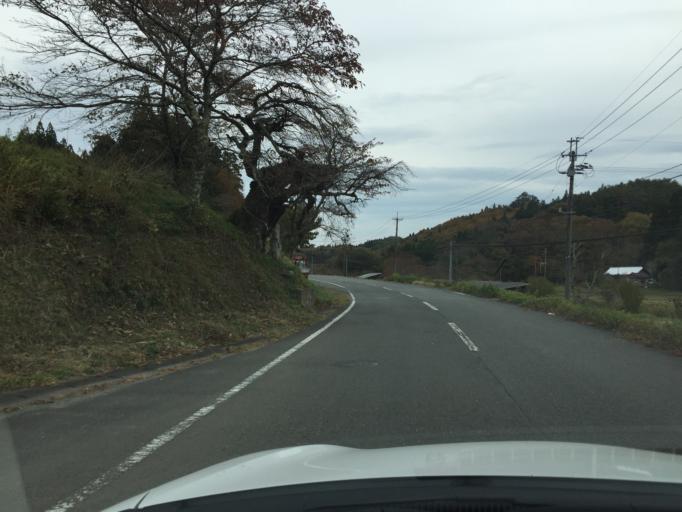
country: JP
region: Fukushima
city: Ishikawa
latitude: 37.2069
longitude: 140.6645
